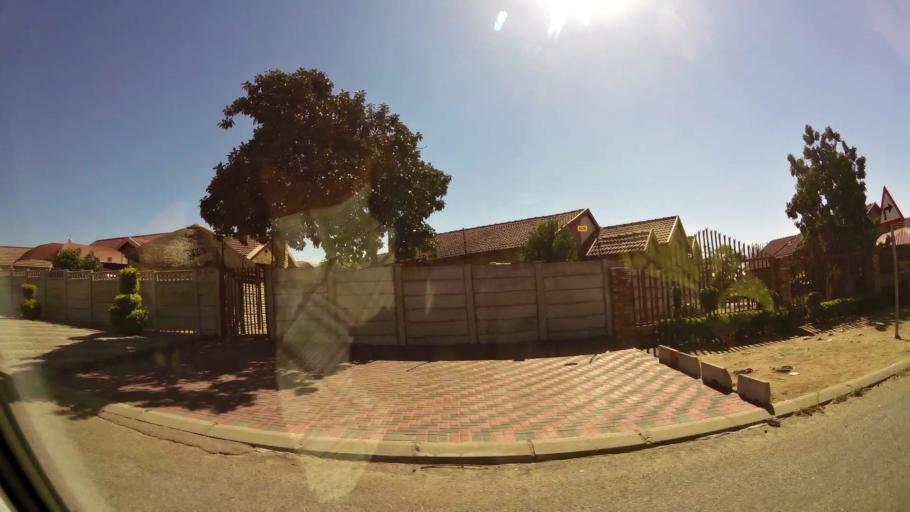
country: ZA
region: Limpopo
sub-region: Capricorn District Municipality
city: Polokwane
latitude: -23.8677
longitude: 29.4302
